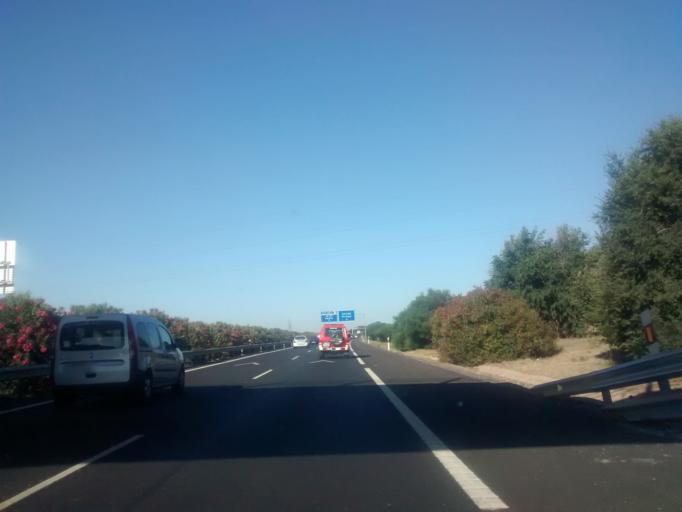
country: ES
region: Andalusia
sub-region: Provincia de Huelva
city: San Juan del Puerto
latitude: 37.3191
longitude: -6.8547
